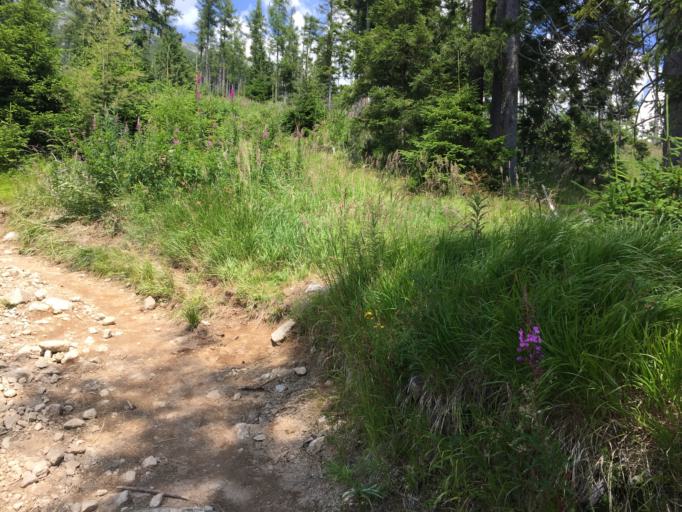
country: SK
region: Presovsky
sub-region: Okres Poprad
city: Vysoke Tatry
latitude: 49.1496
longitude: 20.2092
